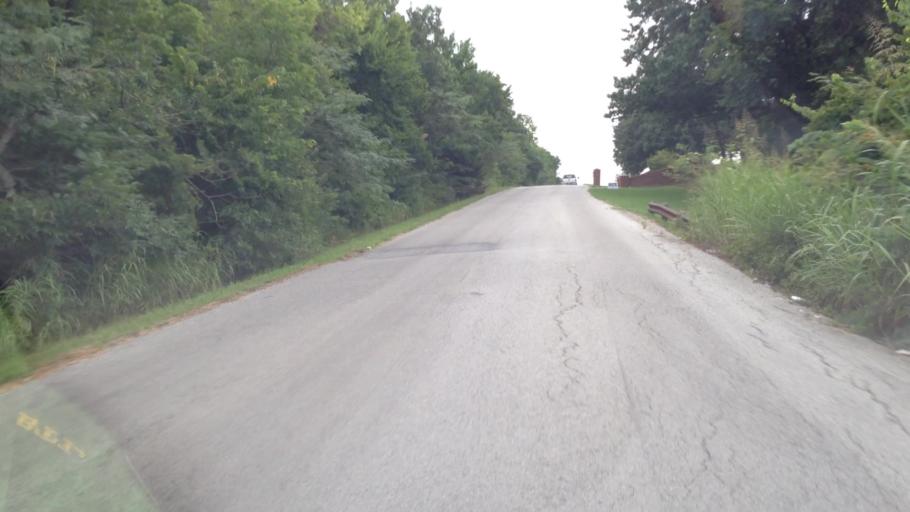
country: US
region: Oklahoma
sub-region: Craig County
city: Vinita
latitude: 36.6276
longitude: -95.1257
